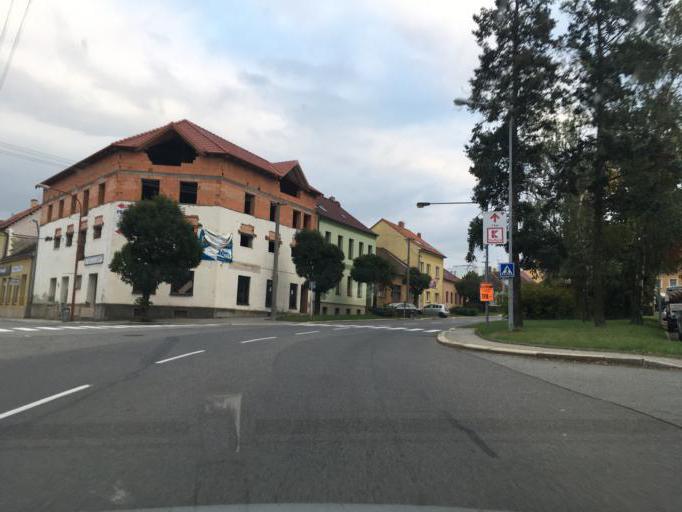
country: CZ
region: Vysocina
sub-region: Okres Trebic
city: Trebic
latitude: 49.2104
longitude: 15.8844
